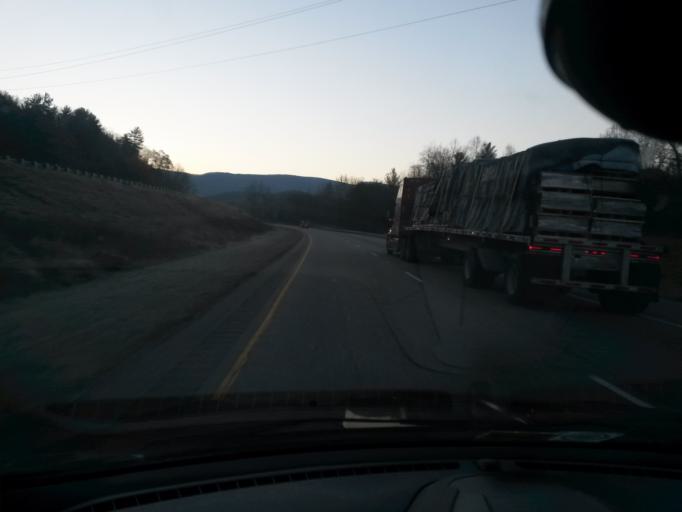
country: US
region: Virginia
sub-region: Alleghany County
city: Clifton Forge
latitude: 37.8004
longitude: -79.7334
